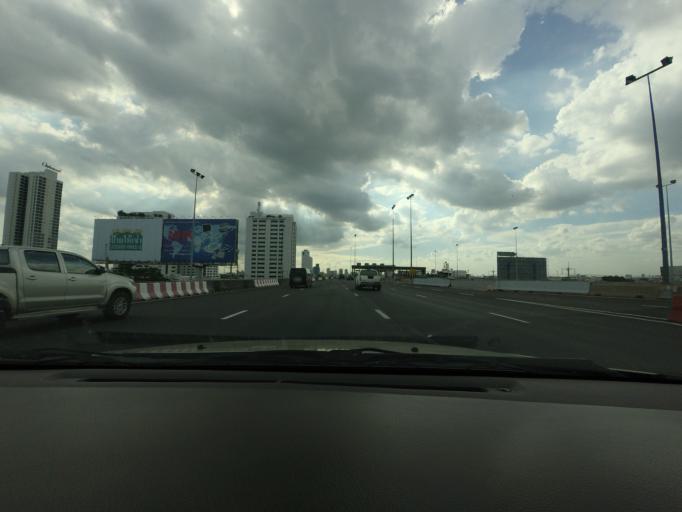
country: TH
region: Bangkok
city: Bang Na
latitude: 13.6592
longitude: 100.6648
